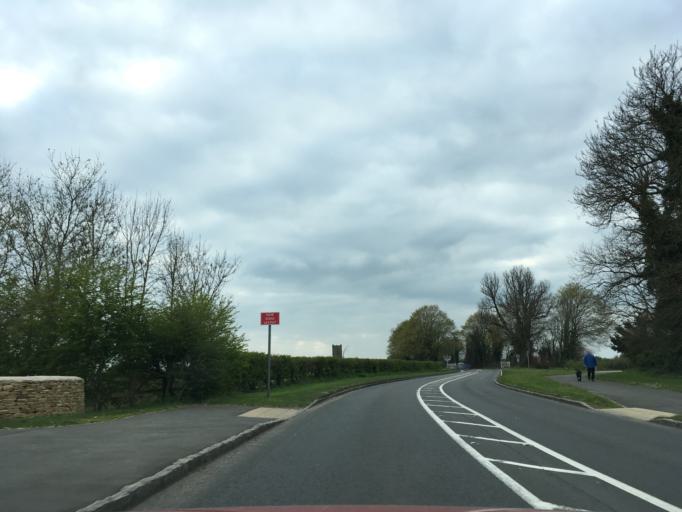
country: GB
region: England
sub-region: Gloucestershire
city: Coates
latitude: 51.6730
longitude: -2.0218
